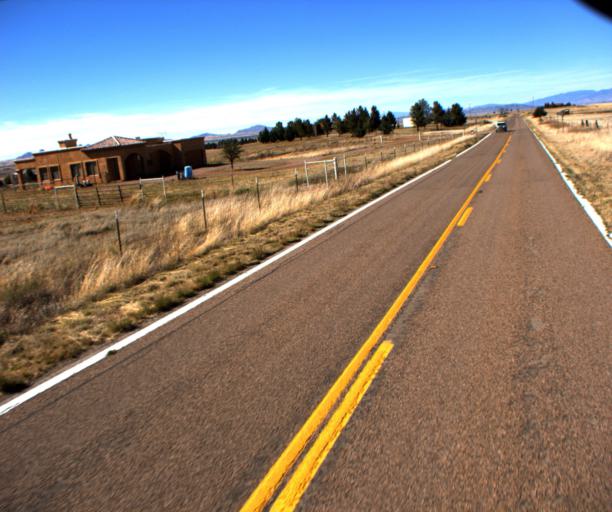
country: US
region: Arizona
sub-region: Cochise County
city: Huachuca City
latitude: 31.6555
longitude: -110.6049
